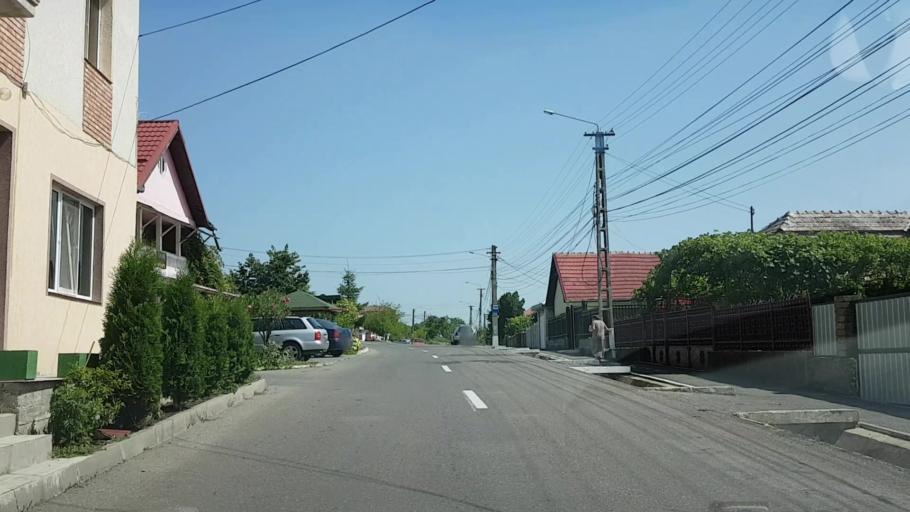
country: RO
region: Cluj
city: Turda
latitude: 46.5791
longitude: 23.7944
